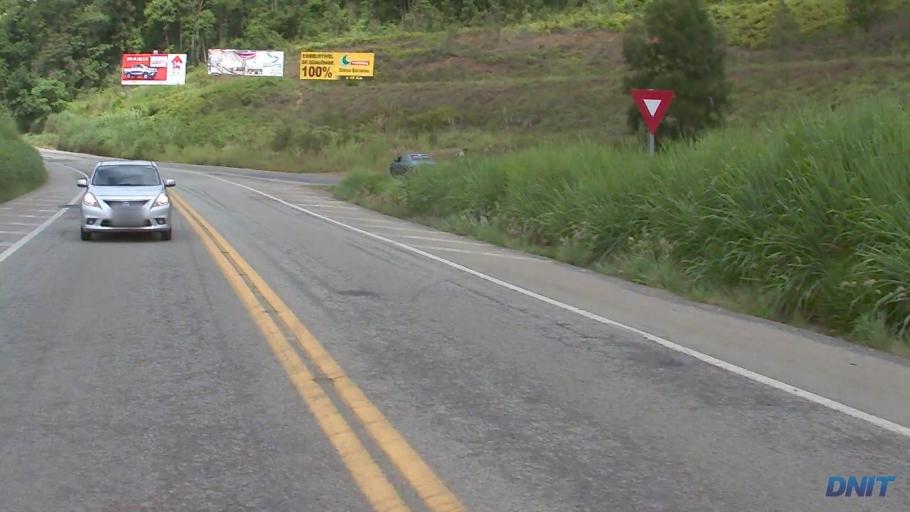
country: BR
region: Minas Gerais
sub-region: Joao Monlevade
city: Joao Monlevade
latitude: -19.8530
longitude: -43.1368
